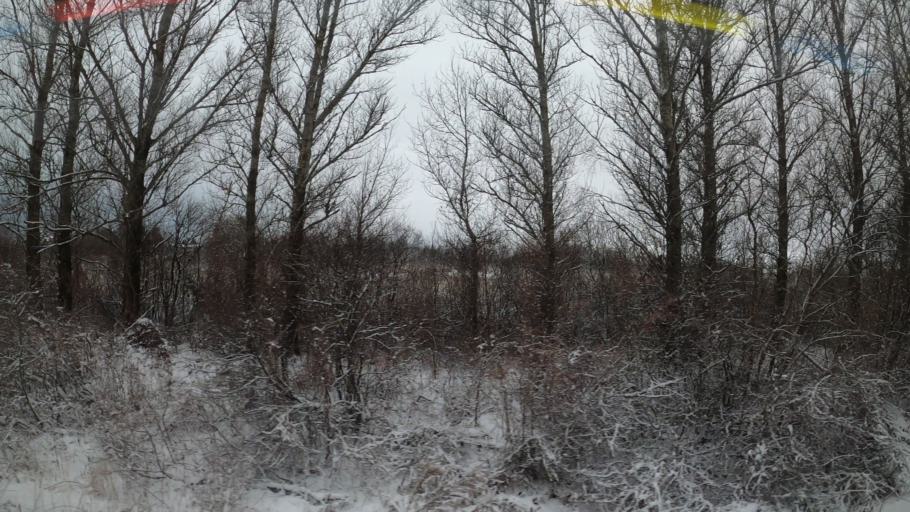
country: RU
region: Jaroslavl
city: Pereslavl'-Zalesskiy
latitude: 56.7115
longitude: 38.9116
